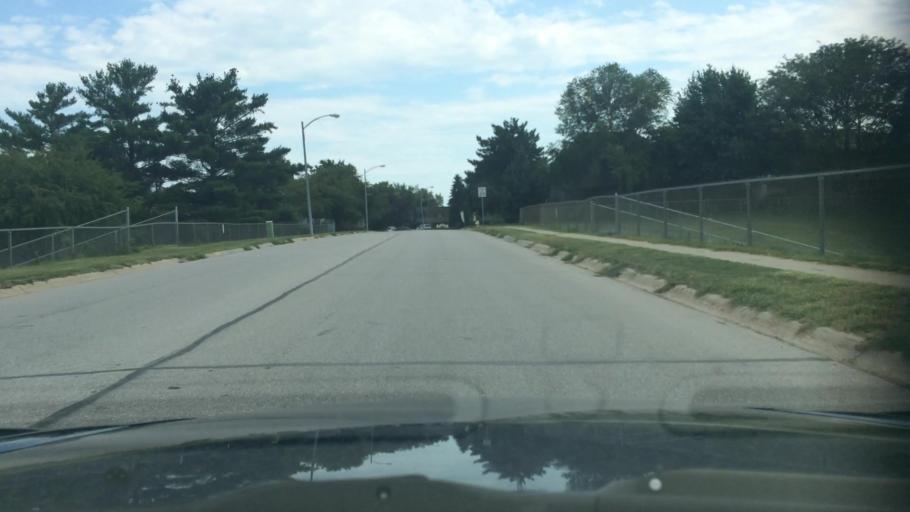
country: US
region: Nebraska
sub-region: Douglas County
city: Ralston
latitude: 41.1974
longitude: -96.0686
